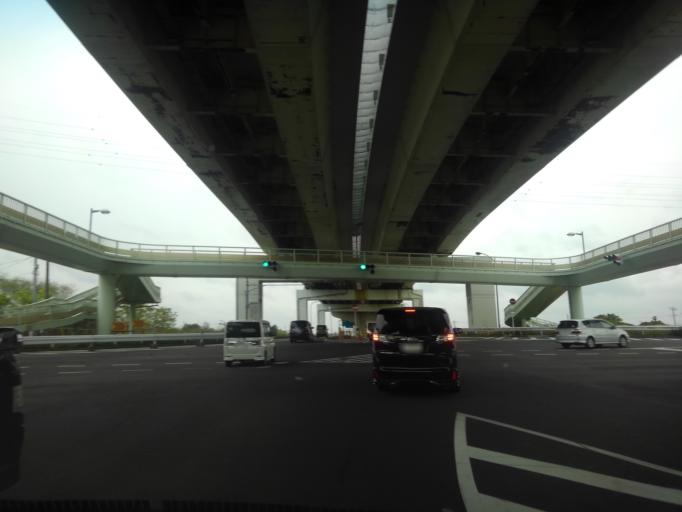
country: JP
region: Chiba
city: Kisarazu
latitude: 35.4132
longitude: 139.9554
